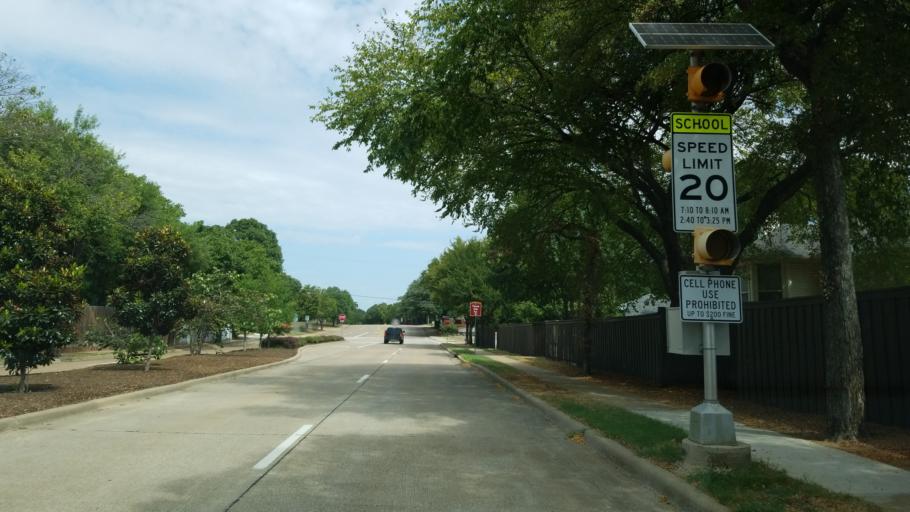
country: US
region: Texas
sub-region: Tarrant County
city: Grapevine
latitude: 32.8880
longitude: -97.0909
